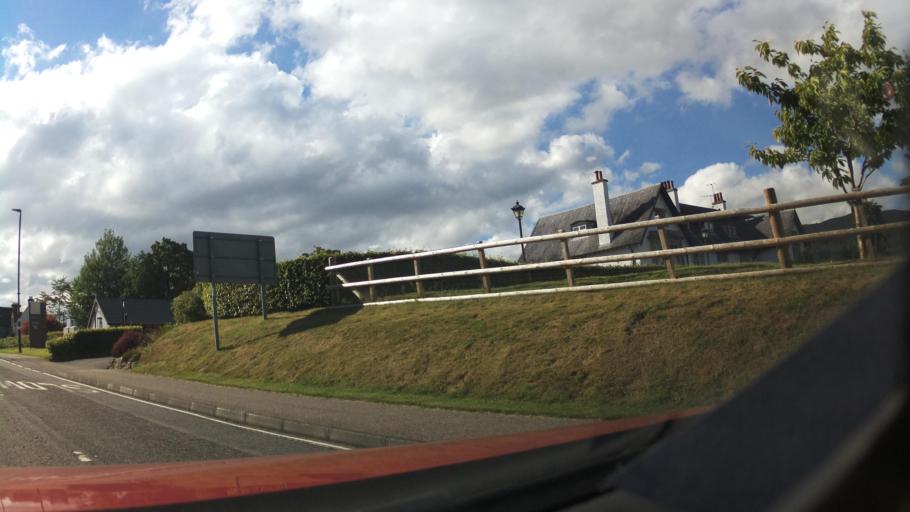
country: GB
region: Scotland
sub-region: Highland
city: Spean Bridge
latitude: 57.1436
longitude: -4.6814
